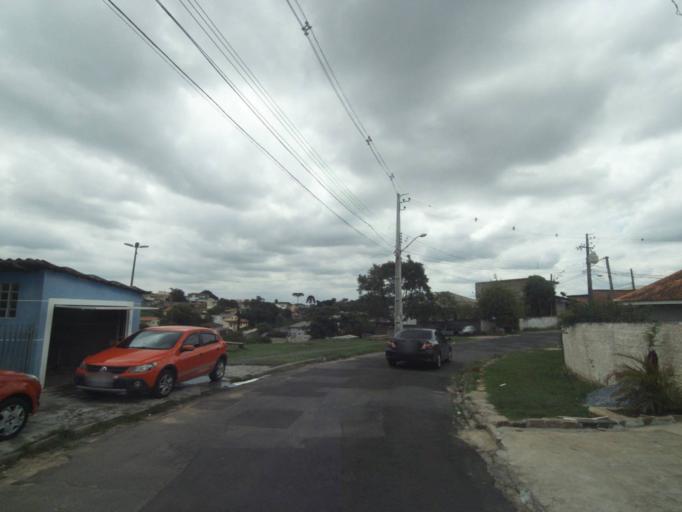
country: BR
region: Parana
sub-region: Curitiba
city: Curitiba
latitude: -25.3896
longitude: -49.2848
